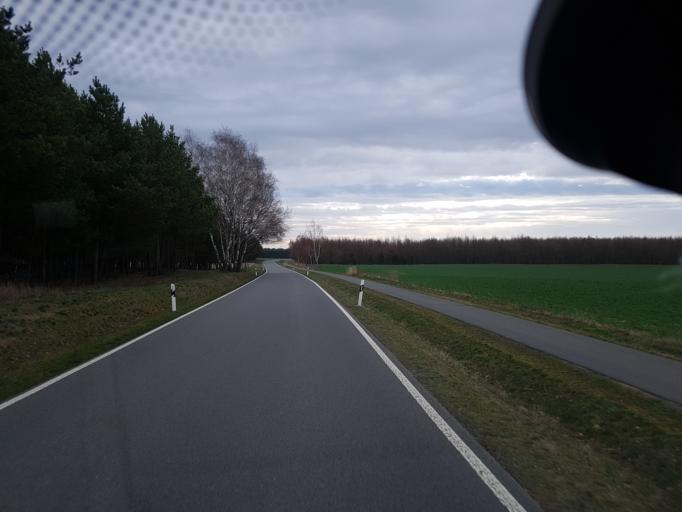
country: DE
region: Brandenburg
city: Mixdorf
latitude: 52.2030
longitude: 14.3634
